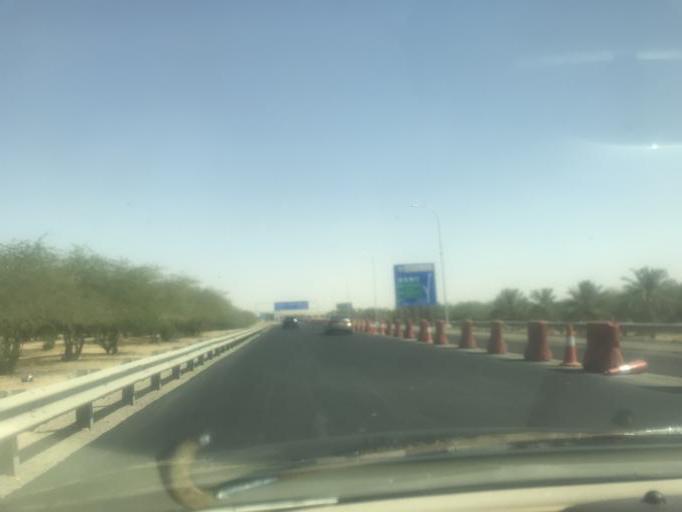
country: SA
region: Ar Riyad
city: Riyadh
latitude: 24.8940
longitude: 46.7146
